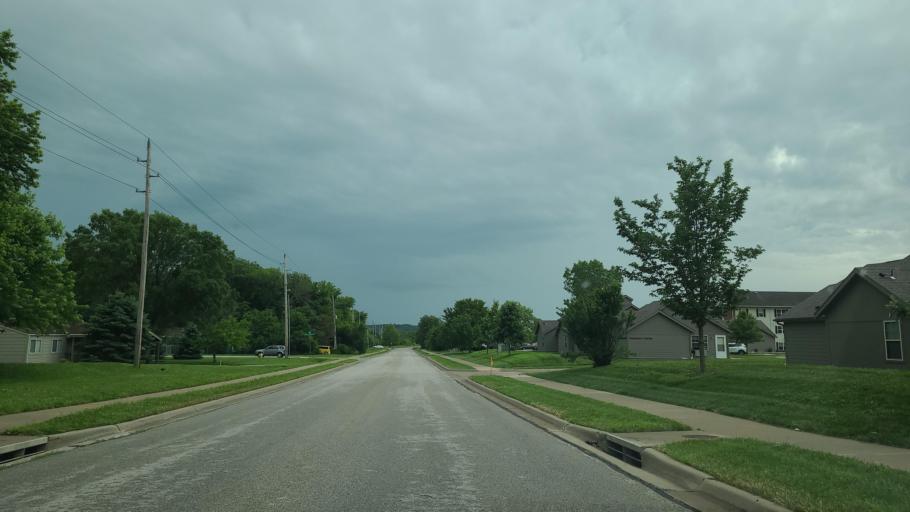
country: US
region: Kansas
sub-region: Douglas County
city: Lawrence
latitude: 38.9396
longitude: -95.2886
